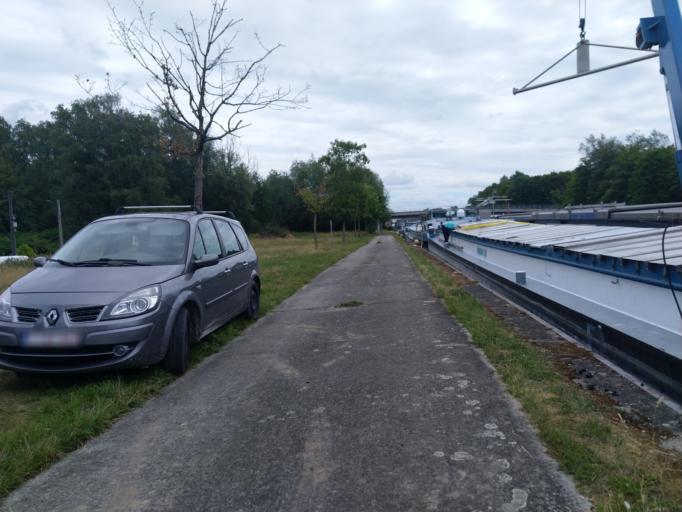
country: BE
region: Wallonia
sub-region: Province du Hainaut
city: Bernissart
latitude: 50.4931
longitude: 3.6540
